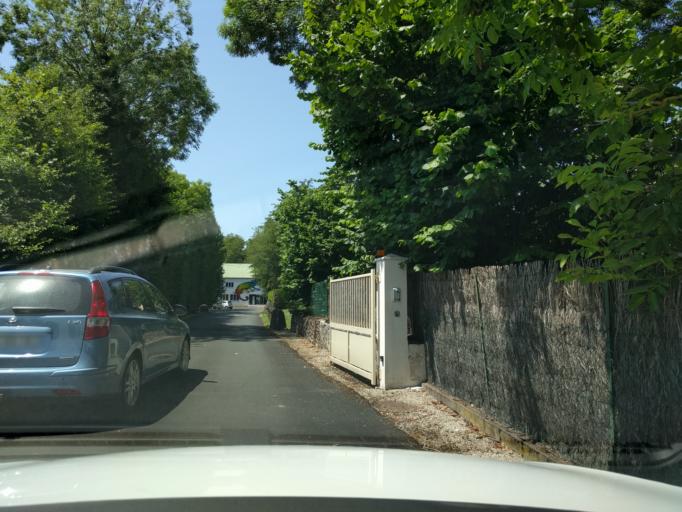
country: FR
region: Poitou-Charentes
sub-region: Departement des Deux-Sevres
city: Niort
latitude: 46.3395
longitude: -0.4754
